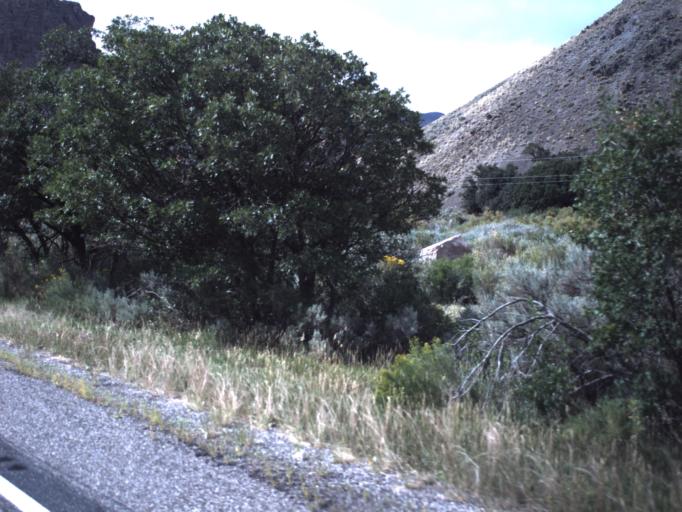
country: US
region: Utah
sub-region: Sevier County
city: Monroe
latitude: 38.4959
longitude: -112.2534
